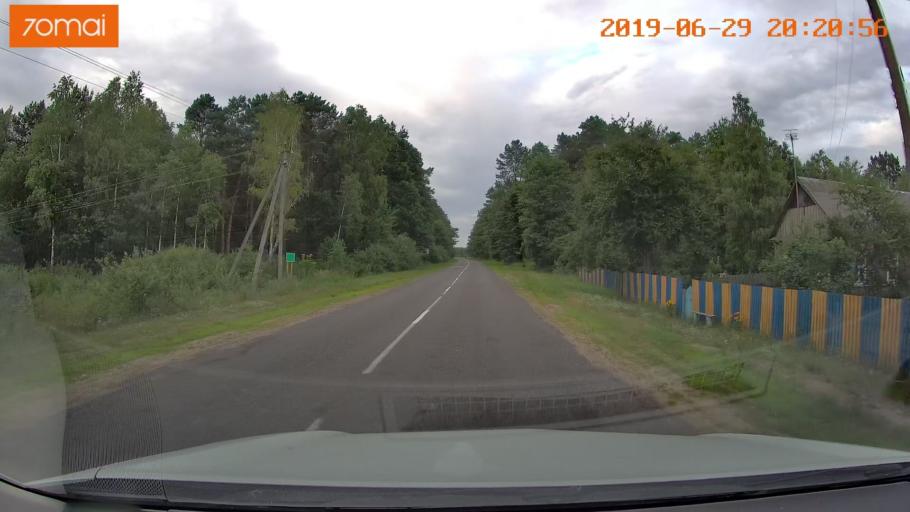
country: BY
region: Brest
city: Asnyezhytsy
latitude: 52.4148
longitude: 26.2512
